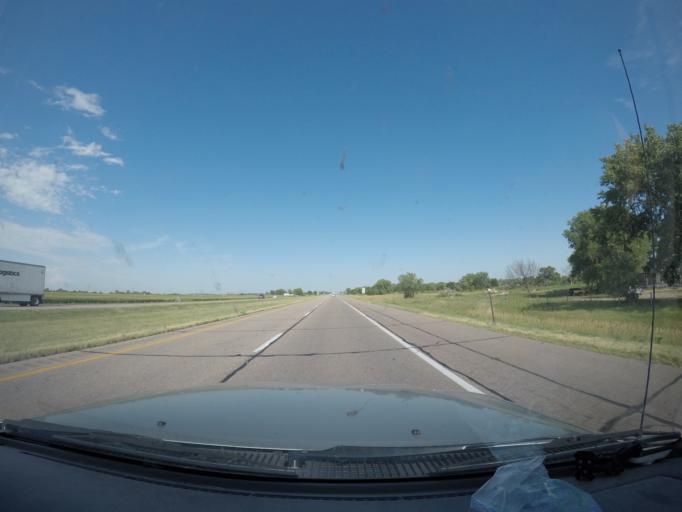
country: US
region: Nebraska
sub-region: Phelps County
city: Holdrege
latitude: 40.6903
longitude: -99.3689
